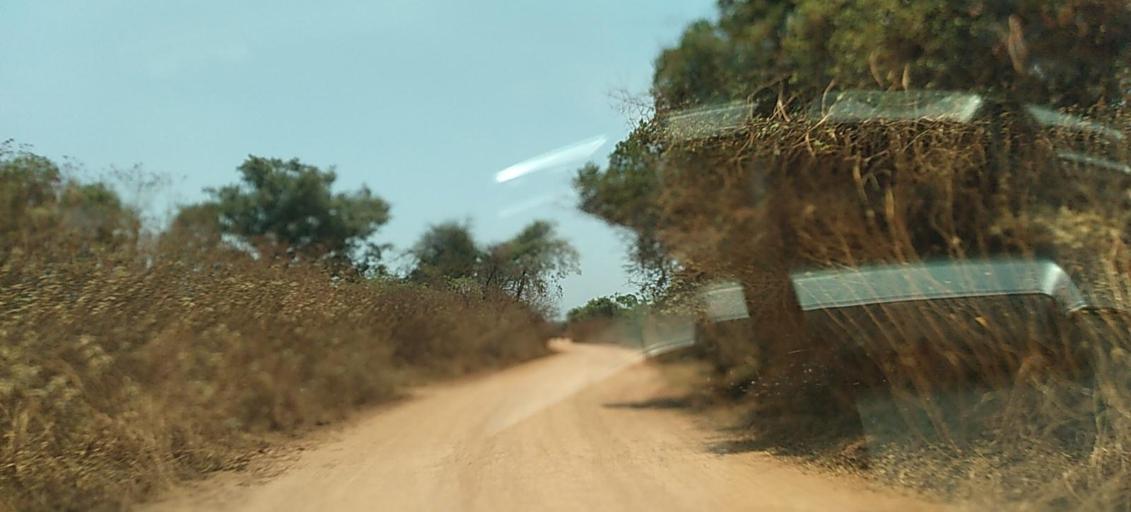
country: CD
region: Katanga
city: Kipushi
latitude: -11.7813
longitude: 27.1844
